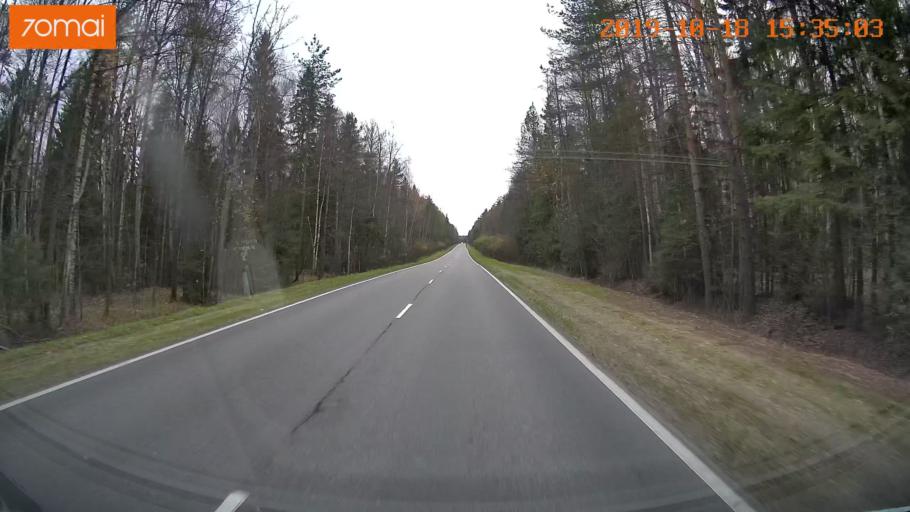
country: RU
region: Vladimir
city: Anopino
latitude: 55.8626
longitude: 40.6356
